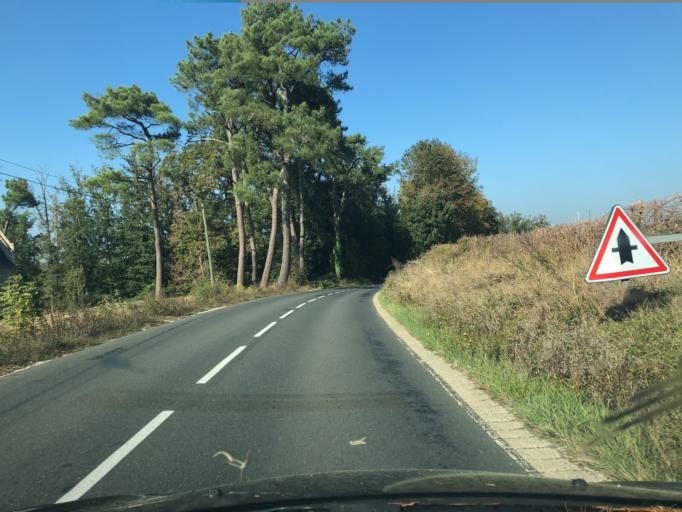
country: FR
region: Centre
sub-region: Departement d'Indre-et-Loire
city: Mettray
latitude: 47.4740
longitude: 0.6638
